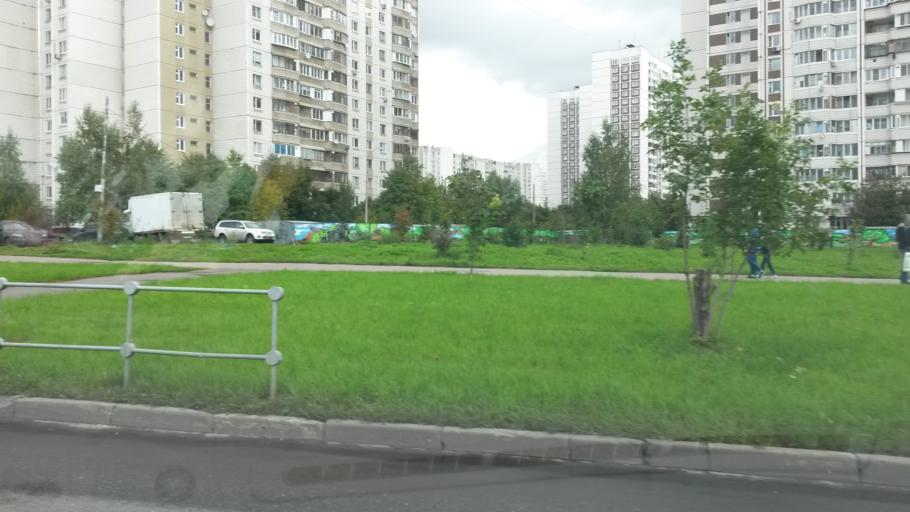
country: RU
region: Moskovskaya
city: Shcherbinka
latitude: 55.5435
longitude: 37.5485
